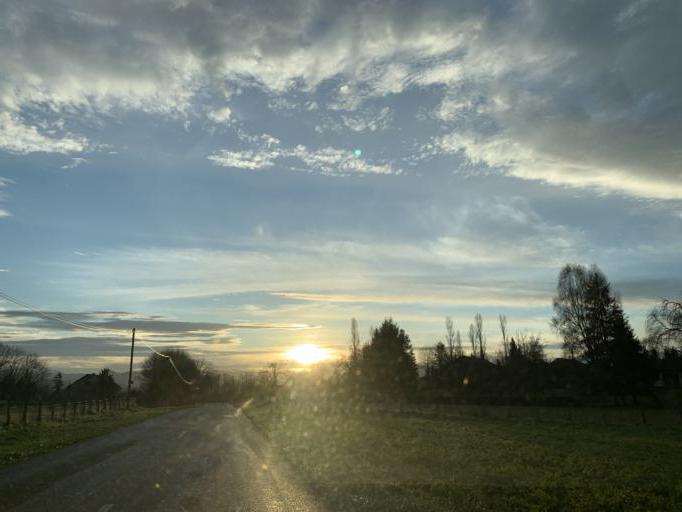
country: FR
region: Rhone-Alpes
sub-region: Departement de l'Ain
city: Belley
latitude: 45.7943
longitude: 5.6390
